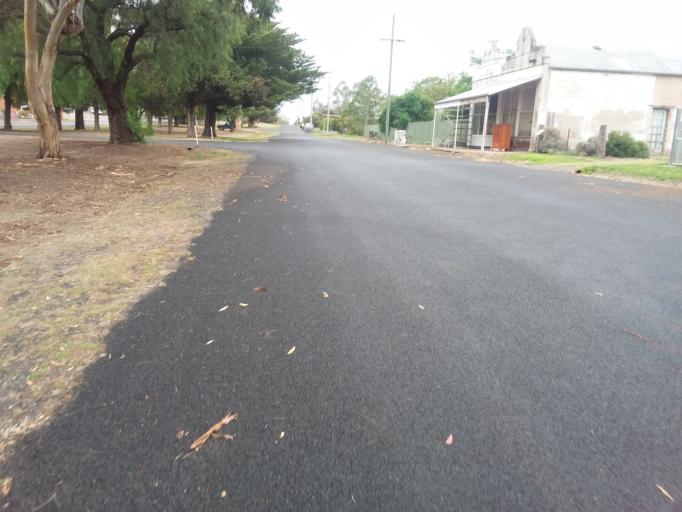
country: AU
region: Victoria
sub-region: Horsham
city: Horsham
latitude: -36.7421
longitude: 141.9403
